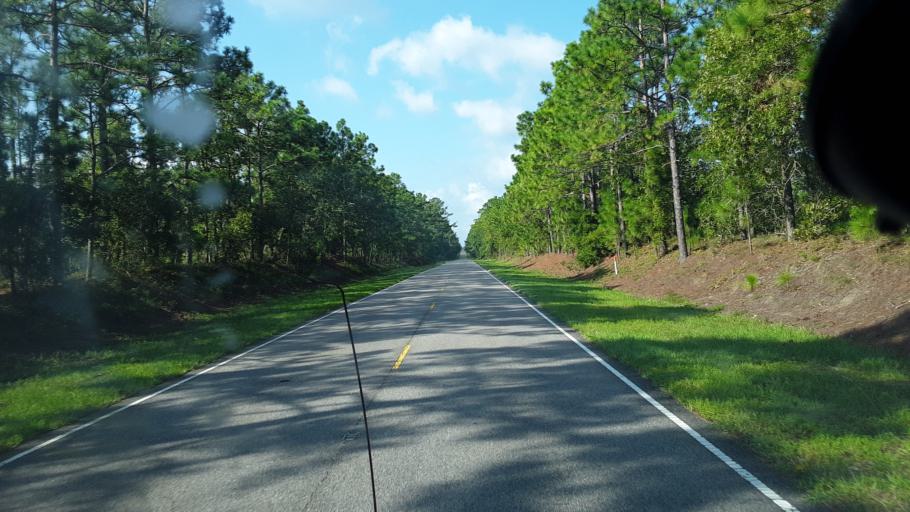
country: US
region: North Carolina
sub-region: Brunswick County
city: Boiling Spring Lakes
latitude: 34.0442
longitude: -78.0030
